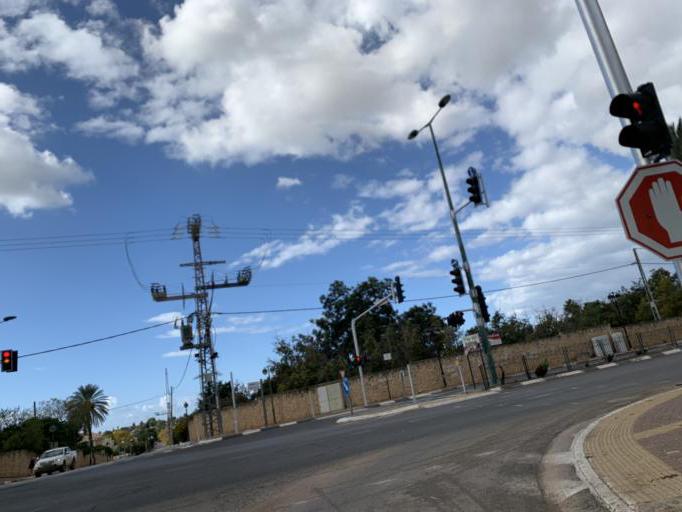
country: IL
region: Central District
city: Hod HaSharon
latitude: 32.1629
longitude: 34.8943
